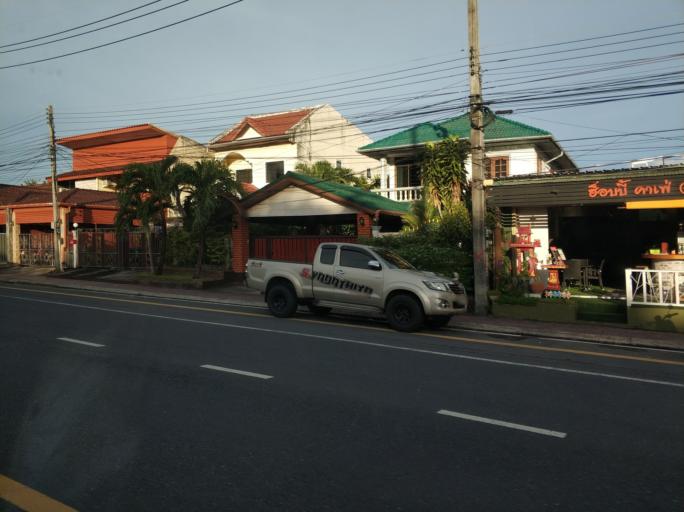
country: TH
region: Phuket
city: Kathu
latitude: 7.9059
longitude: 98.3361
